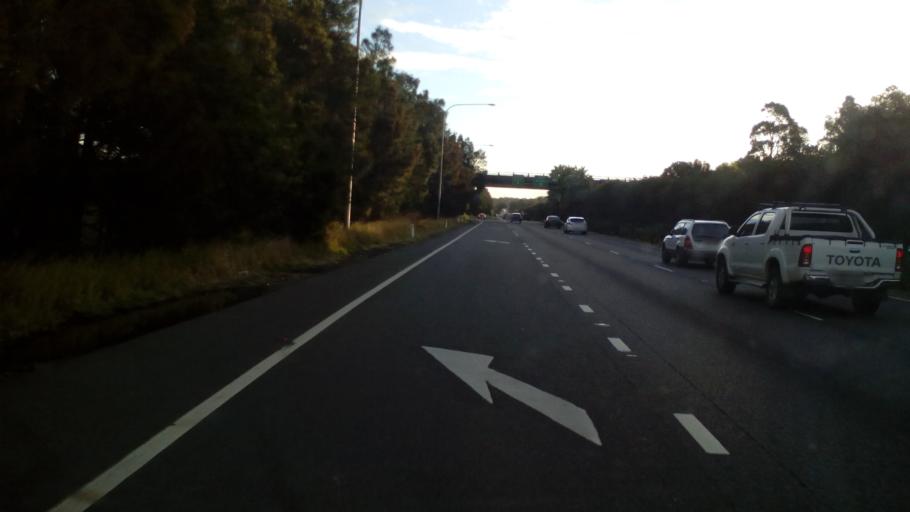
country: AU
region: New South Wales
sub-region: Newcastle
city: Beresfield
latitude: -32.8116
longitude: 151.6674
